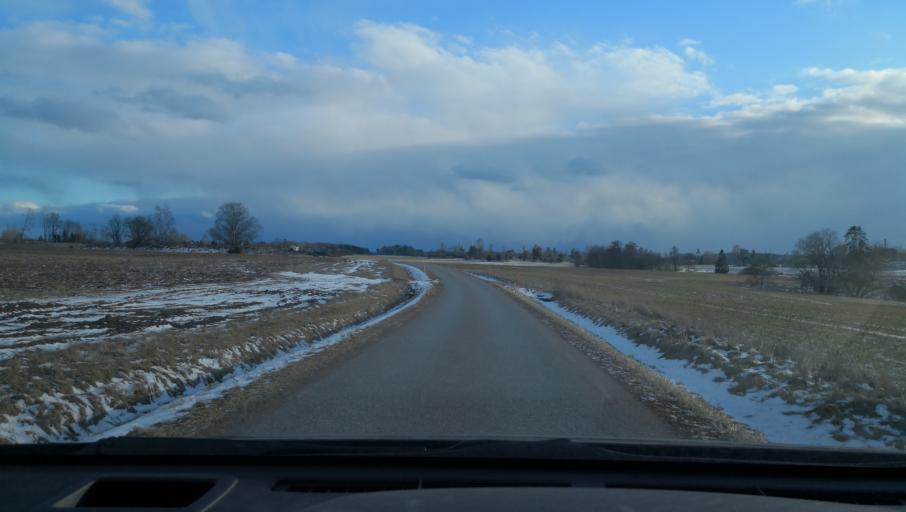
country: SE
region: Uppsala
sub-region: Enkopings Kommun
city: Irsta
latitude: 59.6942
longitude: 16.8587
